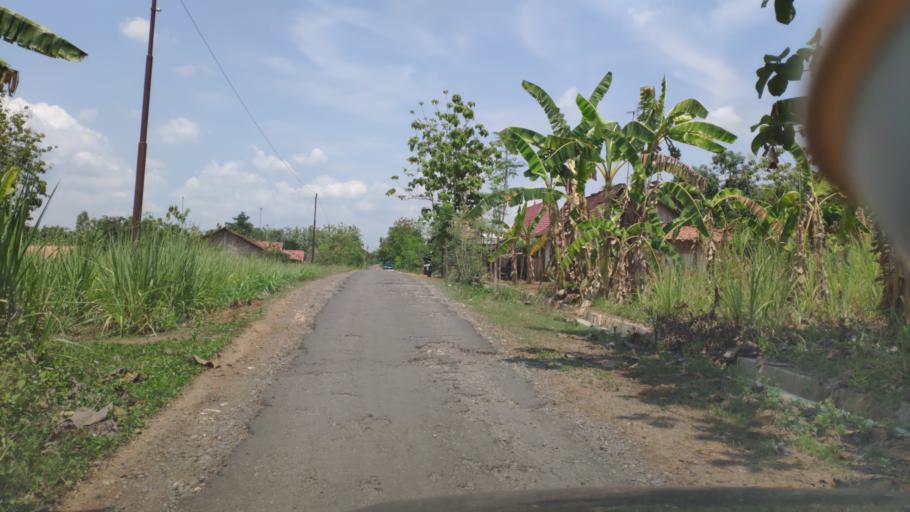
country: ID
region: Central Java
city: Jepang
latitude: -7.0102
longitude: 111.2376
